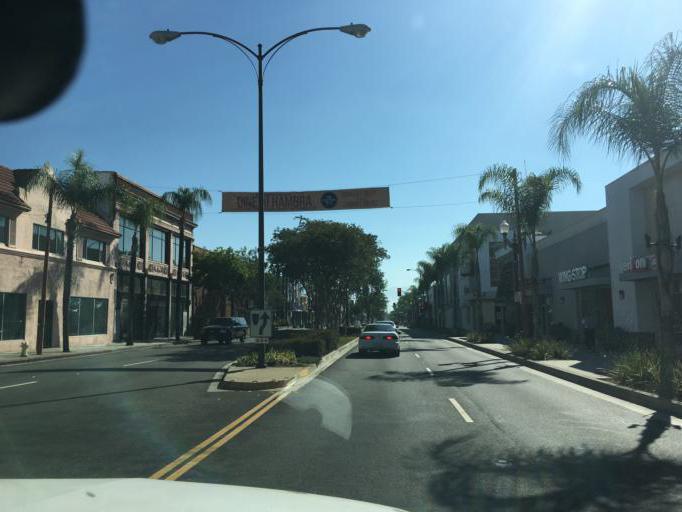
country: US
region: California
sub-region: Los Angeles County
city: Alhambra
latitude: 34.0954
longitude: -118.1263
